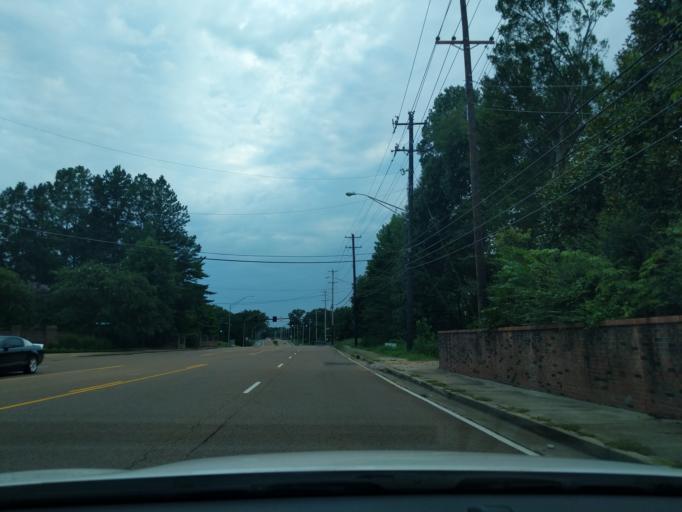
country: US
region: Tennessee
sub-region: Shelby County
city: Germantown
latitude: 35.0789
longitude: -89.8121
